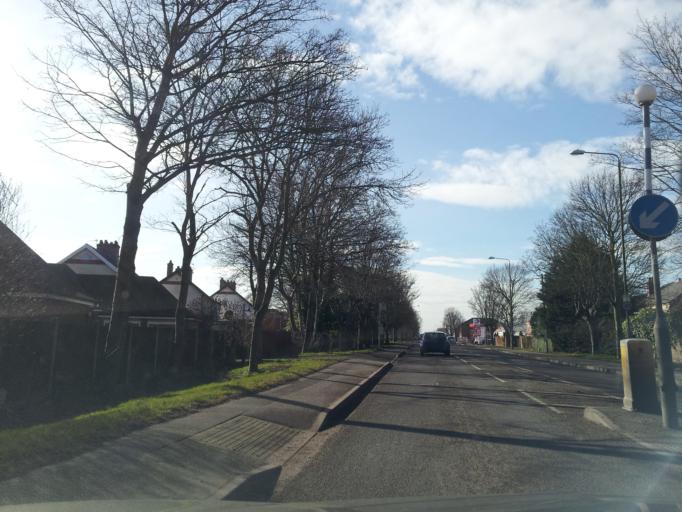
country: GB
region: England
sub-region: Nottinghamshire
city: Newark on Trent
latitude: 53.0676
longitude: -0.8289
